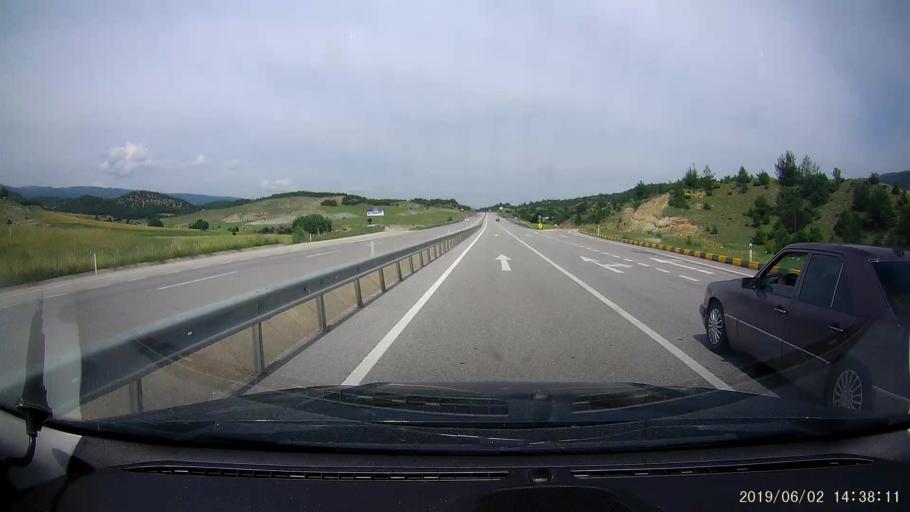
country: TR
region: Corum
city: Hacihamza
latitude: 41.0519
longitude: 34.2743
